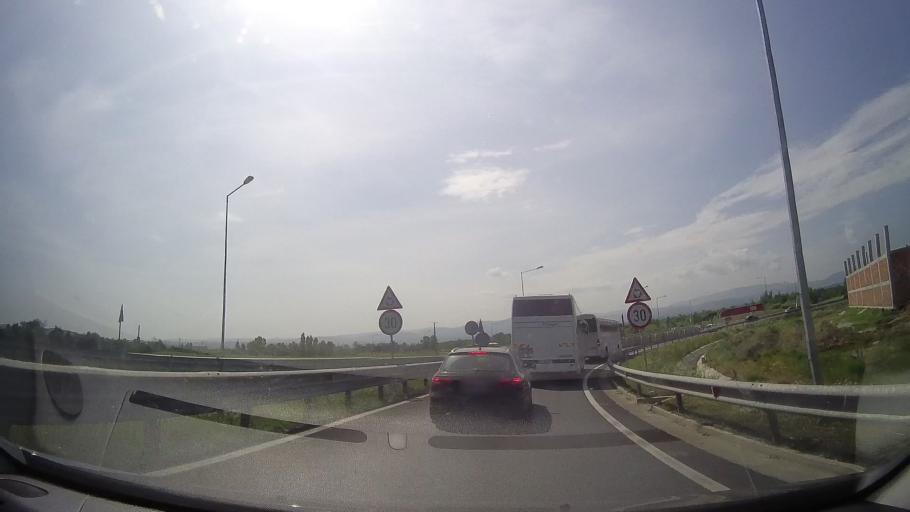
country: RO
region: Timis
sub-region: Comuna Margina
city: Margina
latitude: 45.8595
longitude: 22.2476
